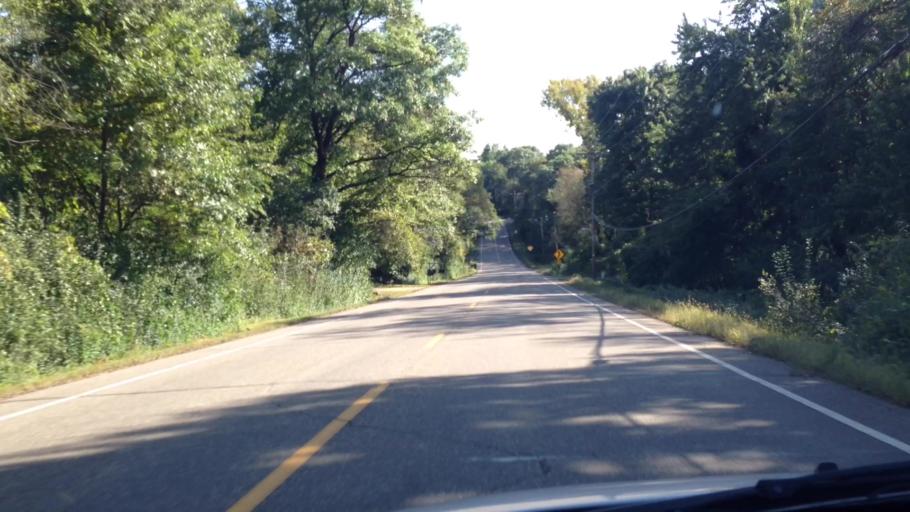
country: US
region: Minnesota
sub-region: Washington County
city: Stillwater
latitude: 45.0857
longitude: -92.8130
